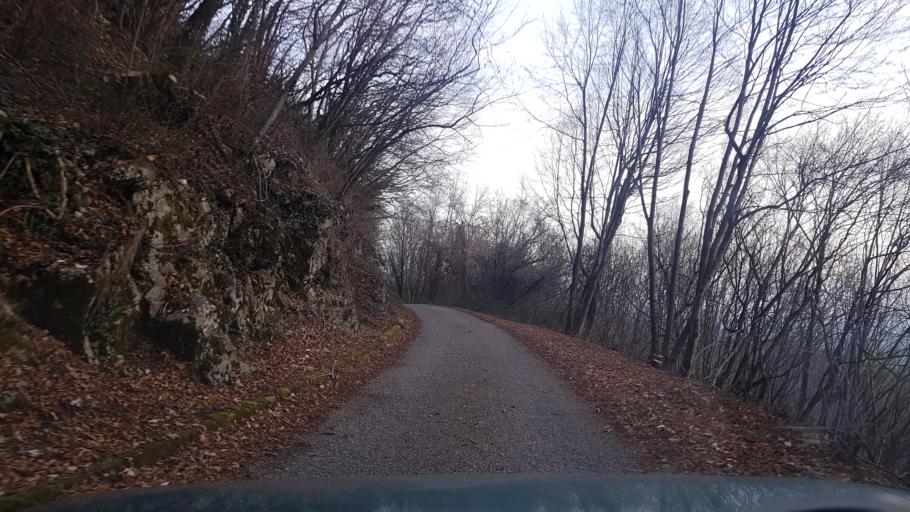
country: IT
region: Friuli Venezia Giulia
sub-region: Provincia di Udine
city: Torreano
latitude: 46.1575
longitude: 13.4479
